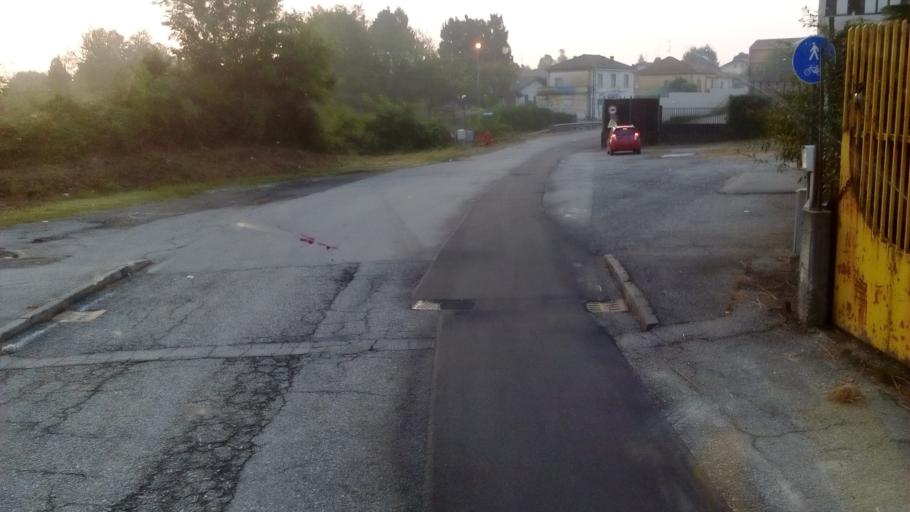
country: IT
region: Piedmont
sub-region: Provincia di Novara
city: Varallo Pombia
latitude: 45.6708
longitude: 8.6191
